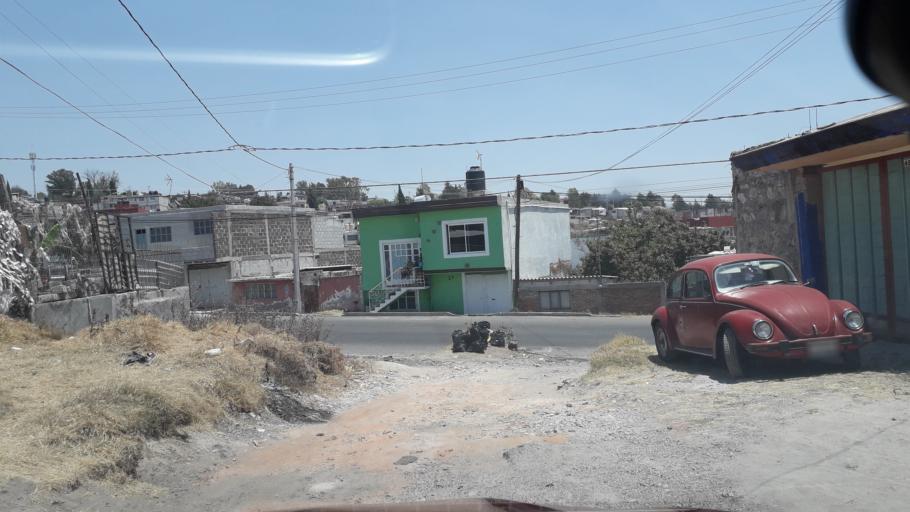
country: MX
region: Puebla
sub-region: Puebla
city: Galaxia la Calera
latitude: 18.9959
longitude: -98.1833
